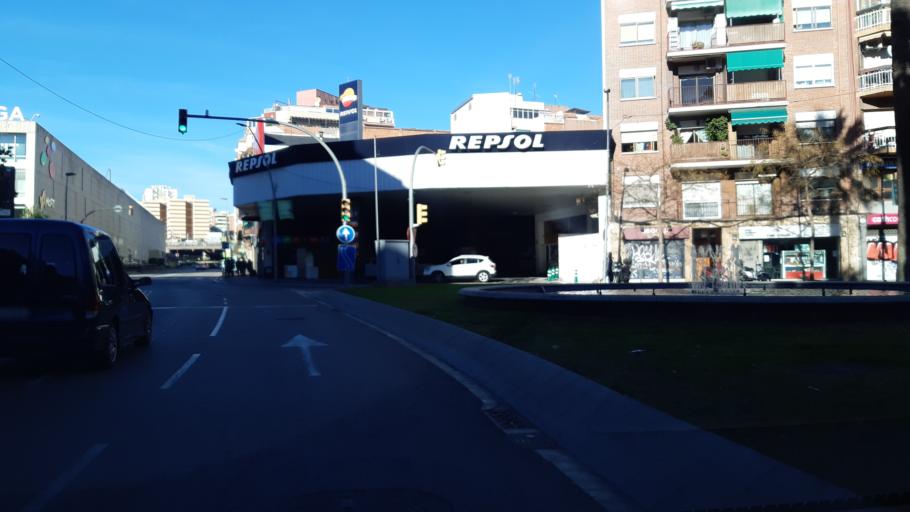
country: ES
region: Catalonia
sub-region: Provincia de Barcelona
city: L'Hospitalet de Llobregat
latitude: 41.3612
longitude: 2.1064
